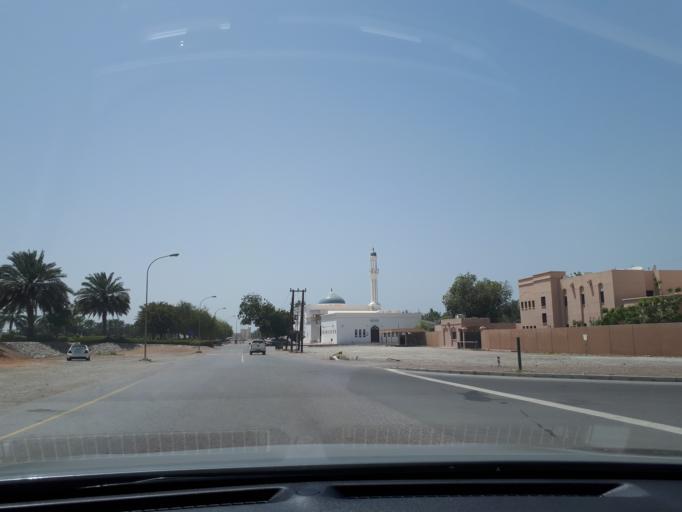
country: OM
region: Muhafazat Masqat
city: As Sib al Jadidah
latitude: 23.6925
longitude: 58.0751
